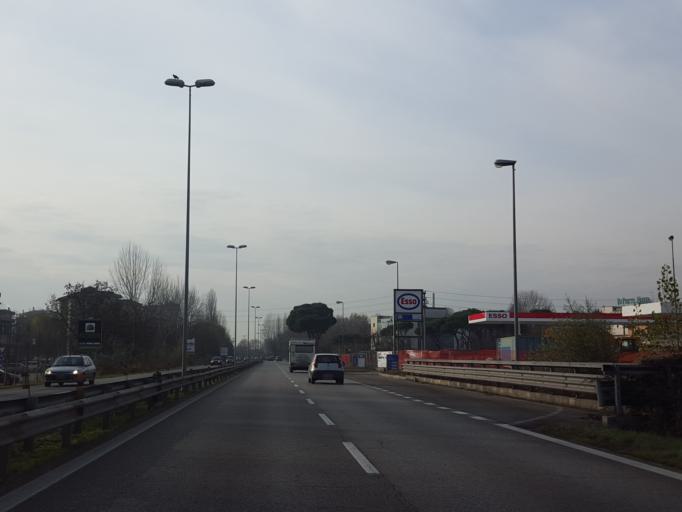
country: IT
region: Veneto
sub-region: Provincia di Vicenza
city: Crispi Cavour
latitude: 45.5518
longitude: 11.5148
